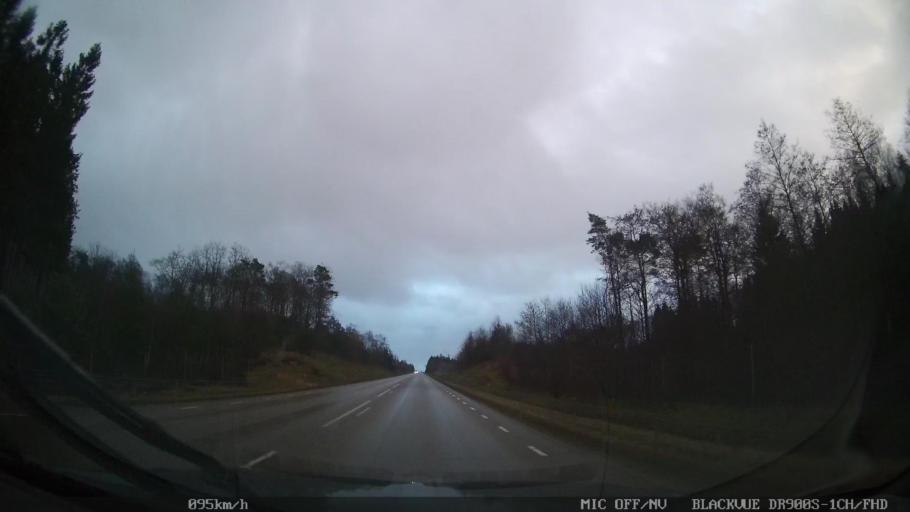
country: SE
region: Skane
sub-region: Orkelljunga Kommun
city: OErkelljunga
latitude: 56.2761
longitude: 13.3487
